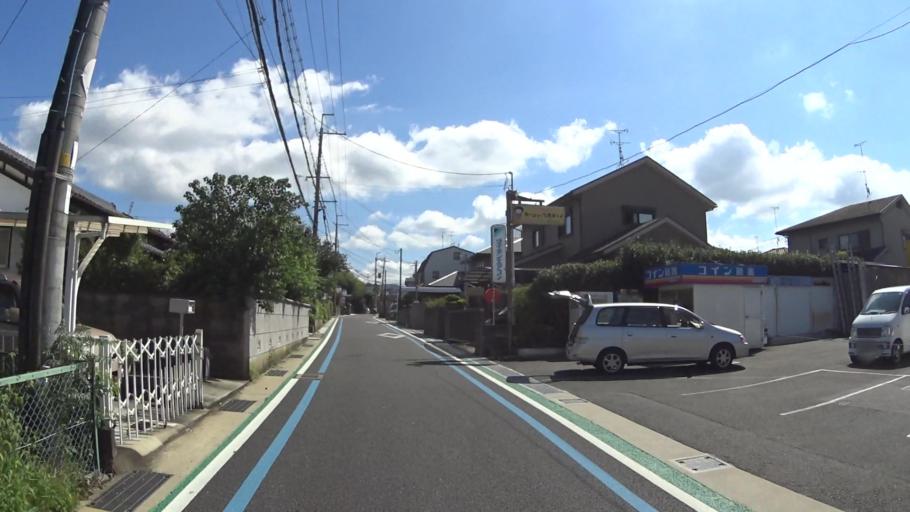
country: JP
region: Kyoto
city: Uji
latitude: 34.8843
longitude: 135.7888
